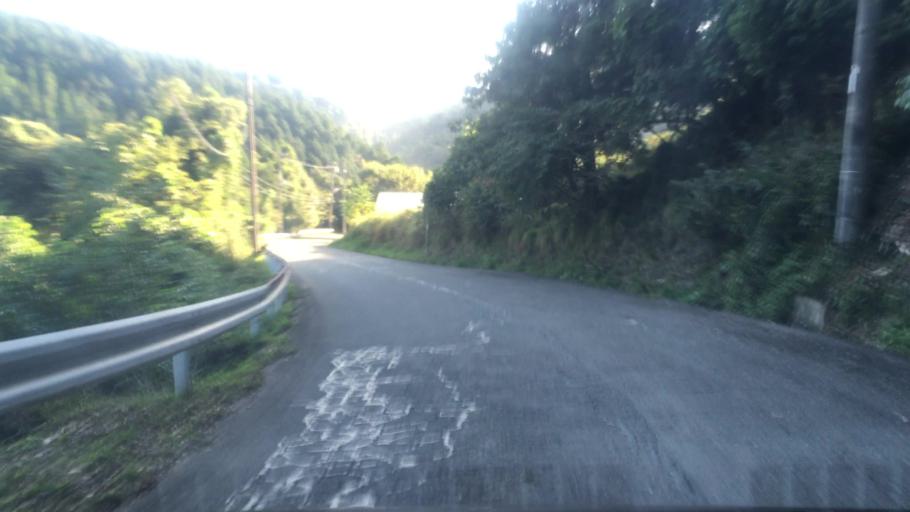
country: JP
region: Hyogo
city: Toyooka
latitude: 35.6108
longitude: 134.8326
